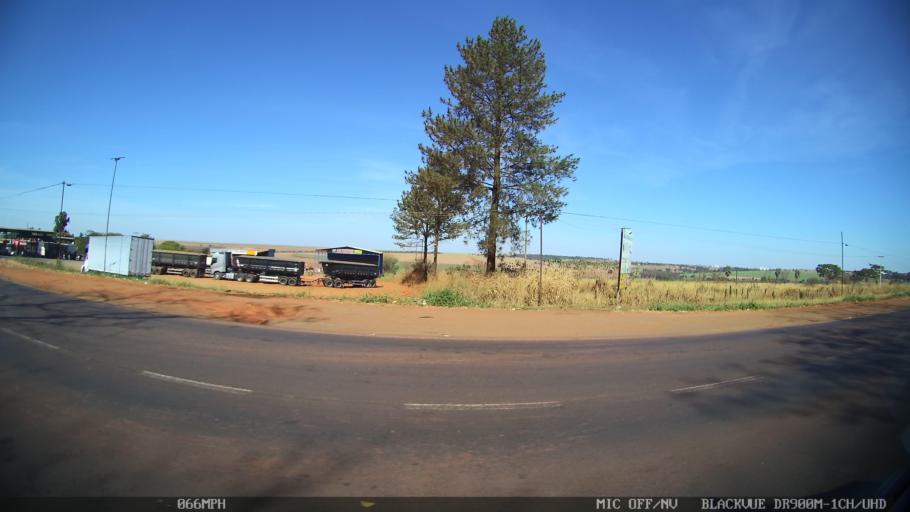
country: BR
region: Sao Paulo
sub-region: Barretos
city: Barretos
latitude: -20.5011
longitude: -48.5416
